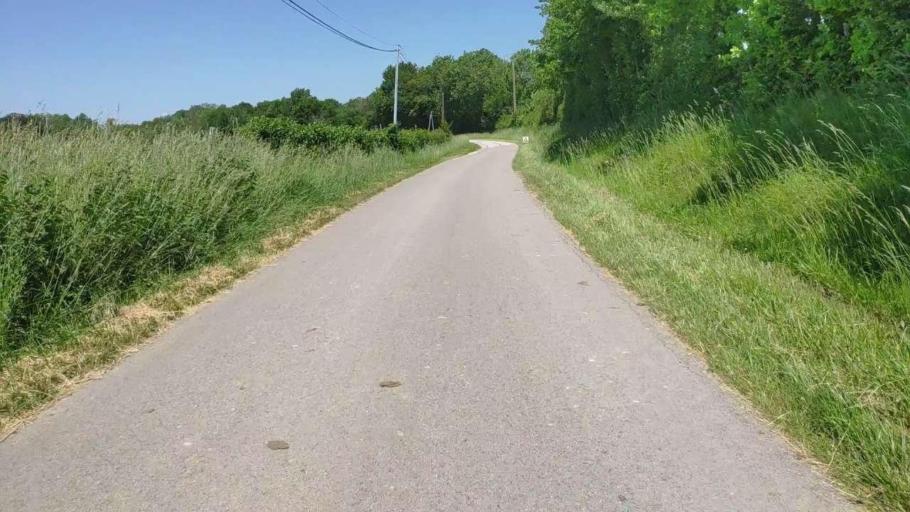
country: FR
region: Franche-Comte
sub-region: Departement du Jura
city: Bletterans
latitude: 46.7575
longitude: 5.4215
